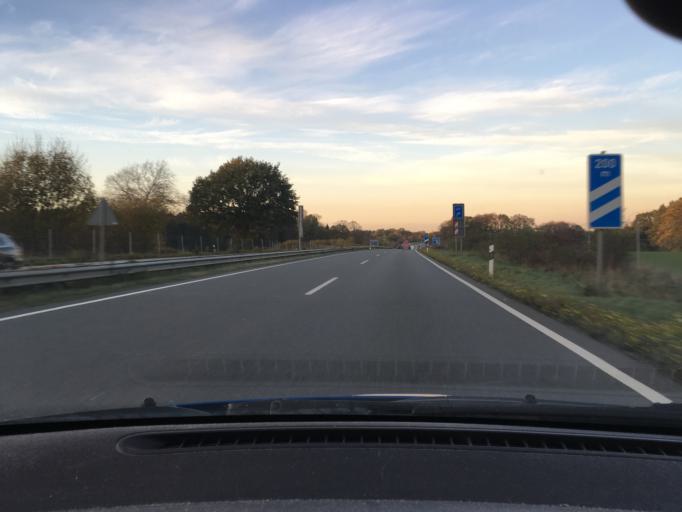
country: DE
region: Schleswig-Holstein
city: Neversdorf
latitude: 53.8521
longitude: 10.3059
